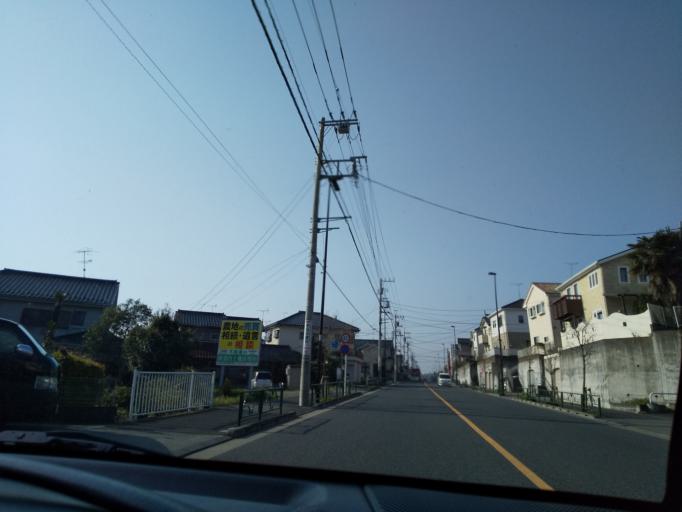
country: JP
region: Tokyo
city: Fussa
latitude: 35.7380
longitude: 139.2903
